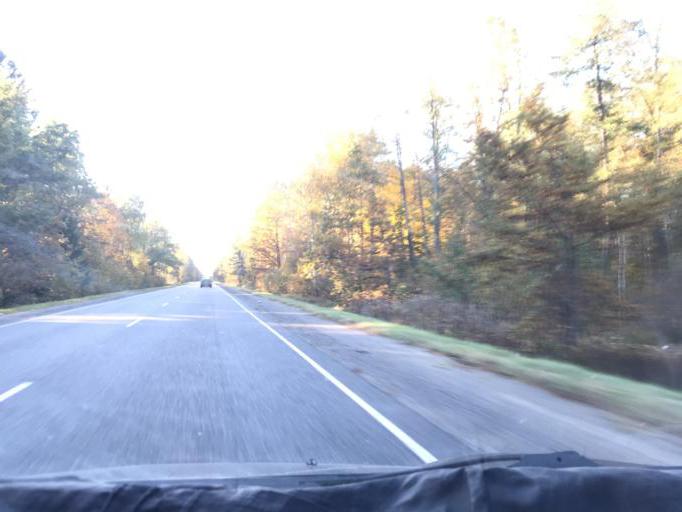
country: BY
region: Gomel
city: Pyetrykaw
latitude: 52.2609
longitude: 28.3263
